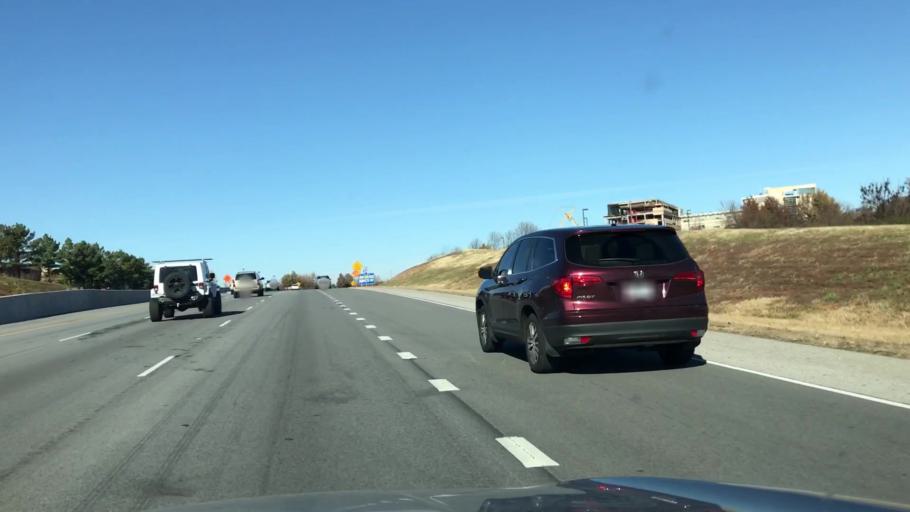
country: US
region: Arkansas
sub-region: Benton County
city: Cave Springs
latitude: 36.3046
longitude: -94.1828
